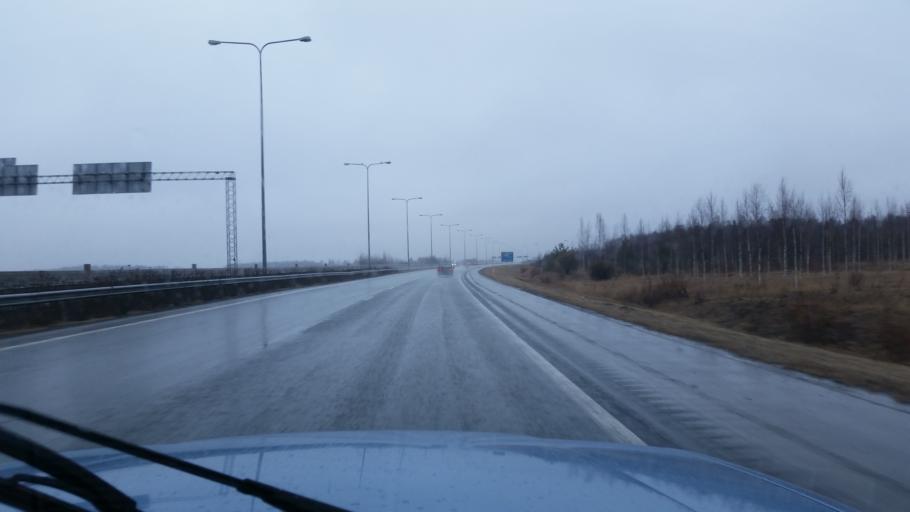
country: FI
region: Pirkanmaa
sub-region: Etelae-Pirkanmaa
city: Toijala
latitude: 61.2074
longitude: 23.8394
